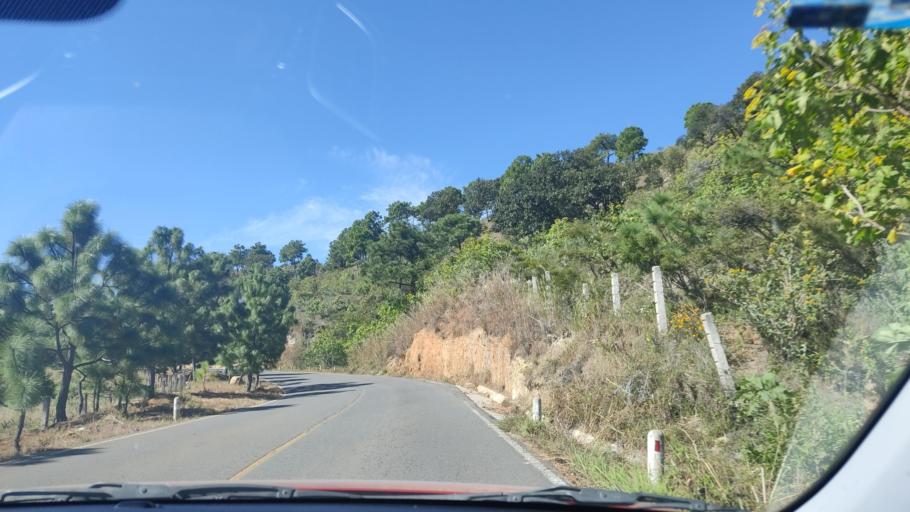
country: MX
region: Nayarit
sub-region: Jala
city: Rosa Blanca
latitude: 21.0971
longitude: -104.3813
